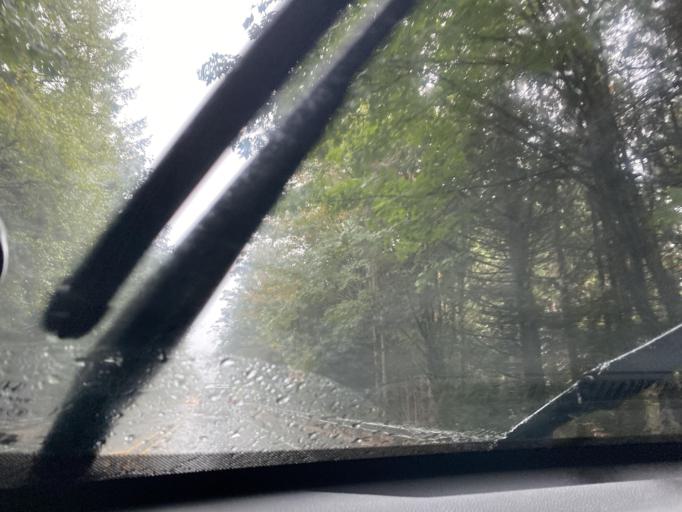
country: US
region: Washington
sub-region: Kitsap County
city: Suquamish
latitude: 47.6836
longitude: -122.5437
